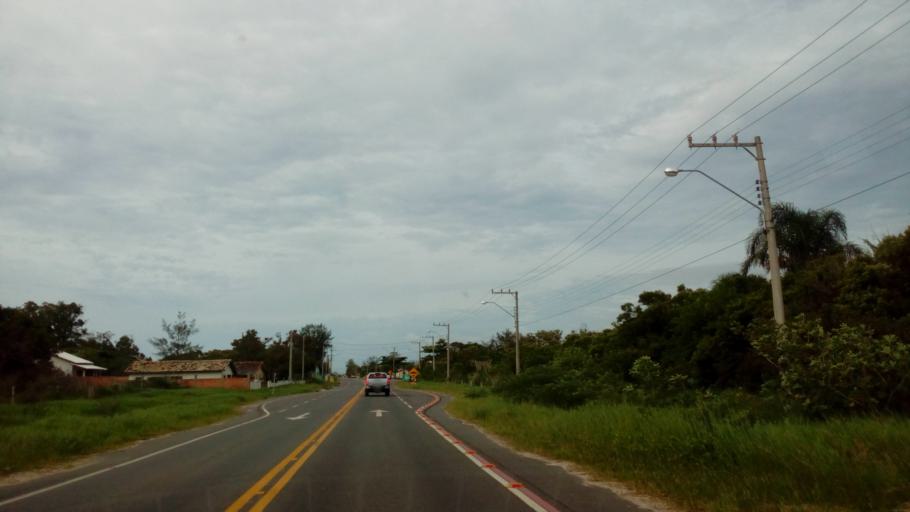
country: BR
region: Santa Catarina
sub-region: Laguna
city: Laguna
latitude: -28.5570
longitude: -48.8027
